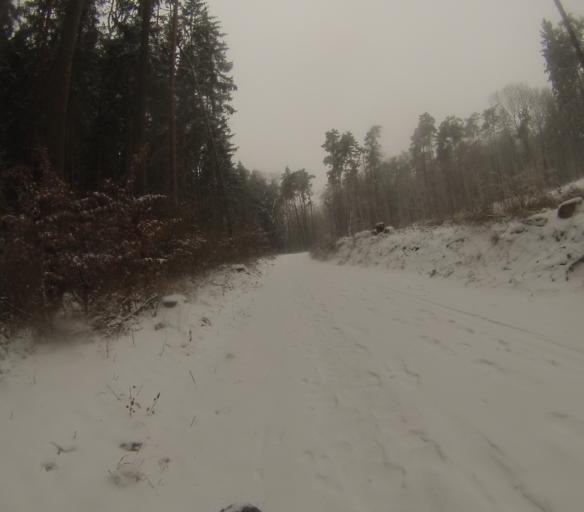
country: CZ
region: South Moravian
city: Strelice
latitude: 49.1375
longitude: 16.4925
